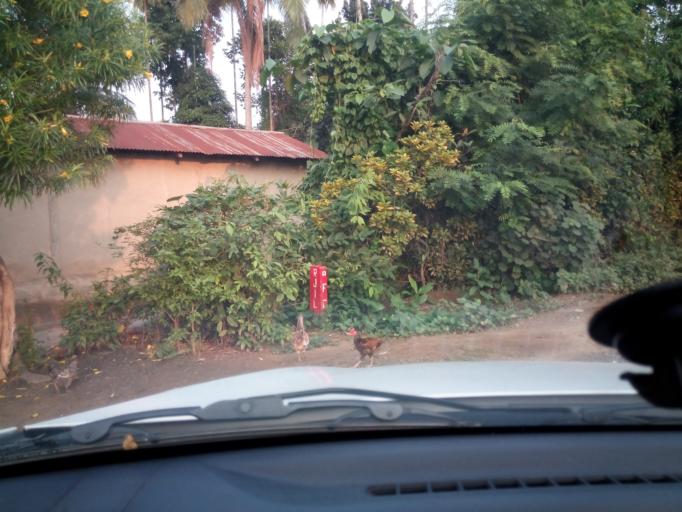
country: IN
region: Assam
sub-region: Udalguri
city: Udalguri
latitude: 26.6757
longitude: 92.0933
